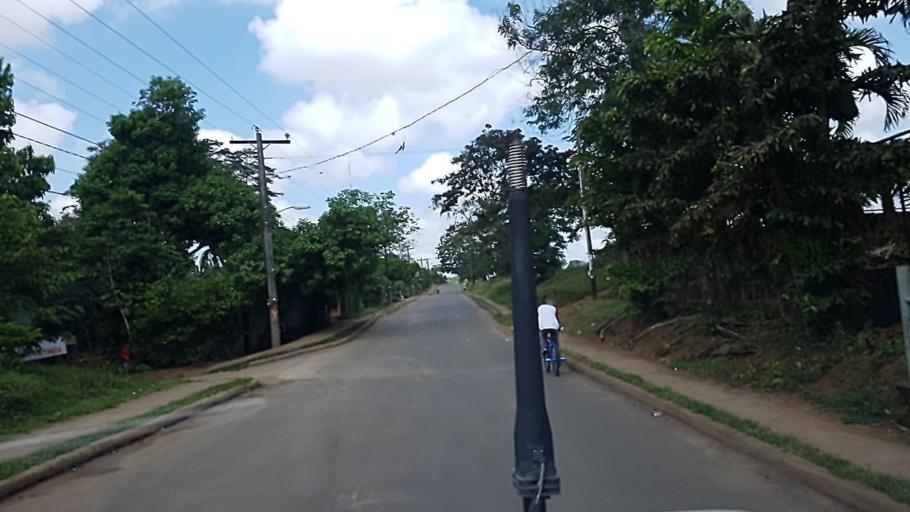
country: NI
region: Atlantico Sur
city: Nueva Guinea
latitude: 11.6870
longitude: -84.4549
